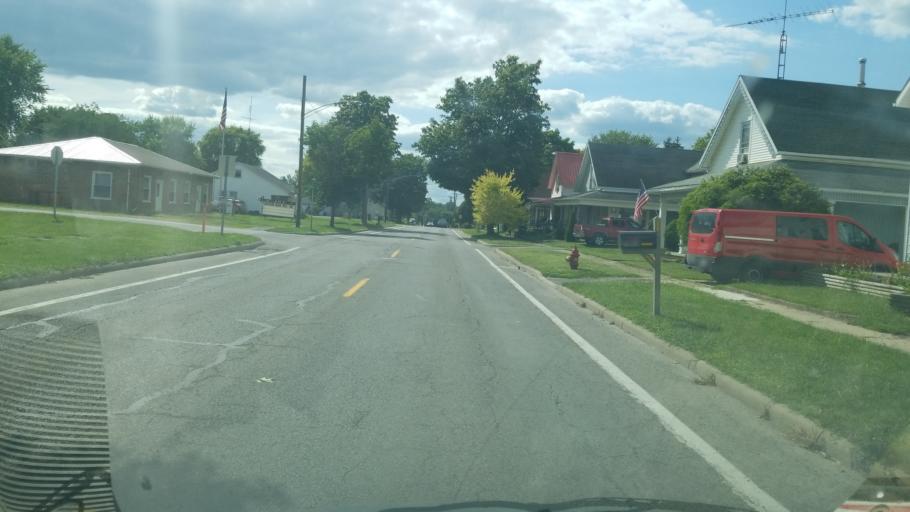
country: US
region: Ohio
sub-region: Logan County
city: De Graff
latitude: 40.3121
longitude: -83.9191
